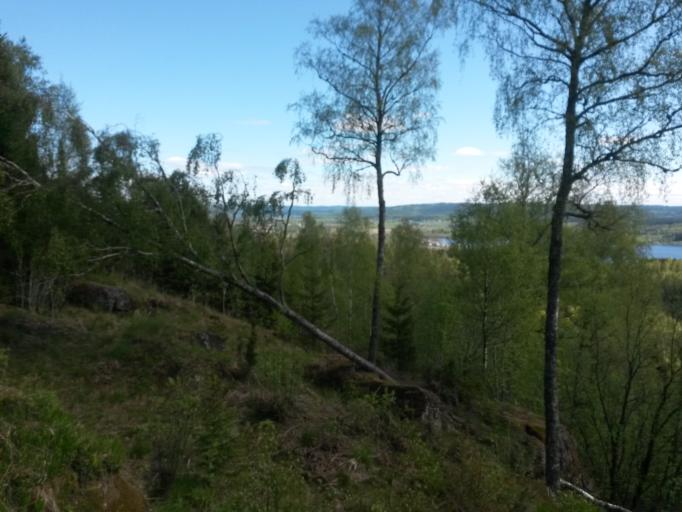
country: SE
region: Vaermland
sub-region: Sunne Kommun
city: Sunne
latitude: 59.8180
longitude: 13.1097
